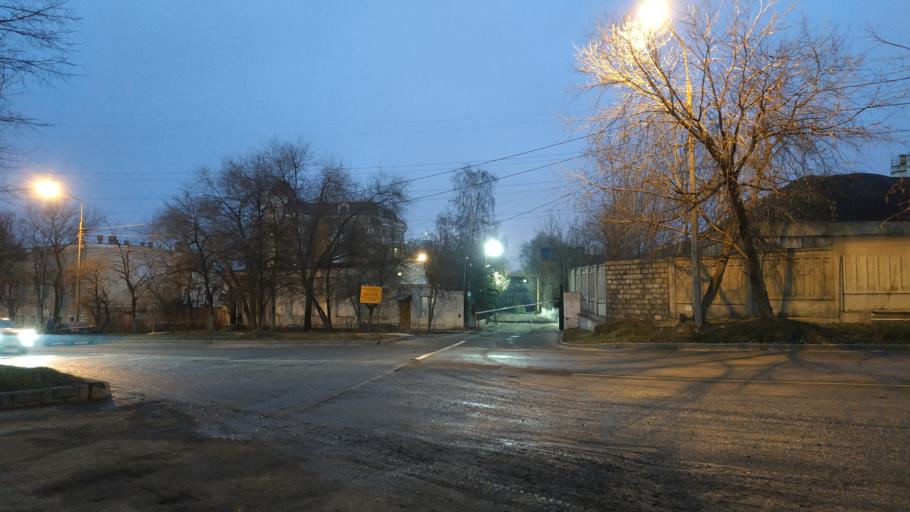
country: RU
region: Moscow
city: Sokol
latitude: 55.7649
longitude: 37.5117
